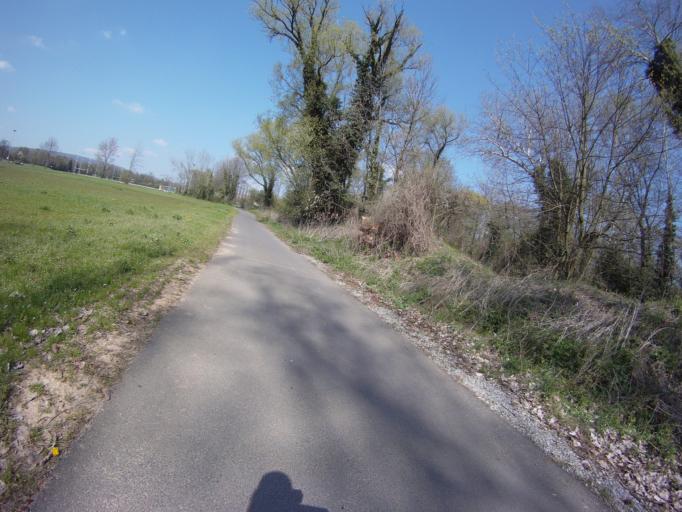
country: FR
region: Lorraine
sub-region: Departement de Meurthe-et-Moselle
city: Blenod-les-Pont-a-Mousson
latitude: 48.8925
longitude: 6.0589
